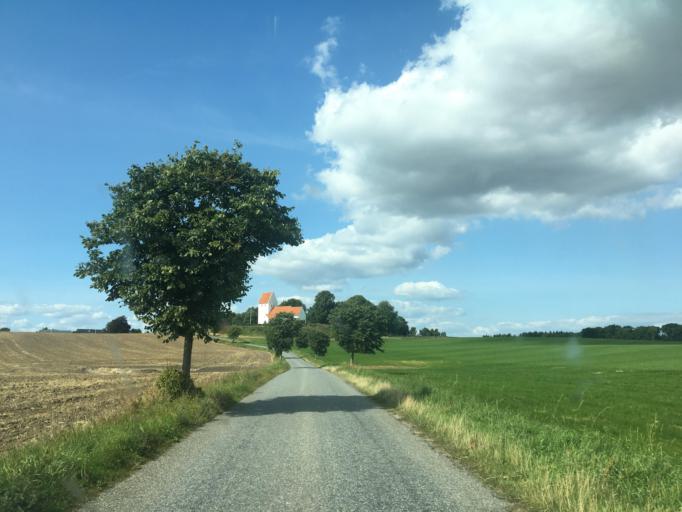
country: DK
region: South Denmark
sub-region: Middelfart Kommune
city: Ejby
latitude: 55.4029
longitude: 9.9172
